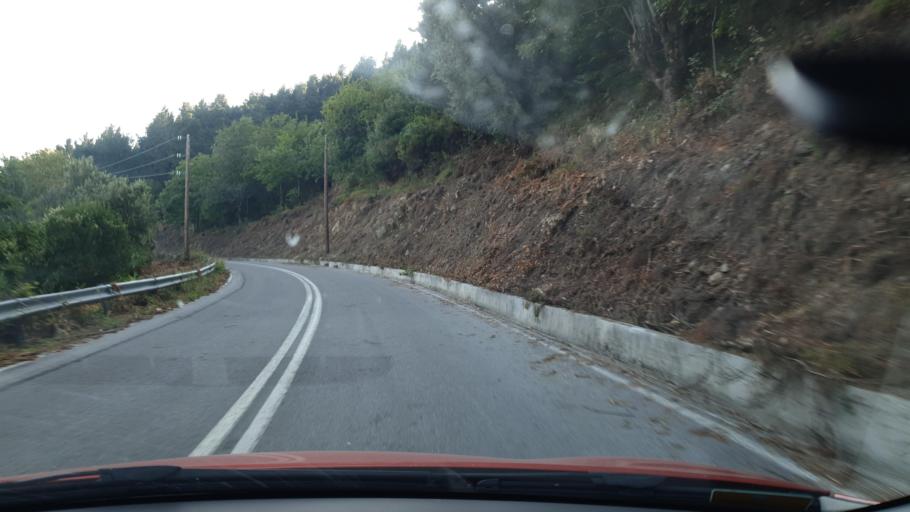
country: GR
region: Central Greece
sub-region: Nomos Evvoias
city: Kymi
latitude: 38.6347
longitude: 23.9356
